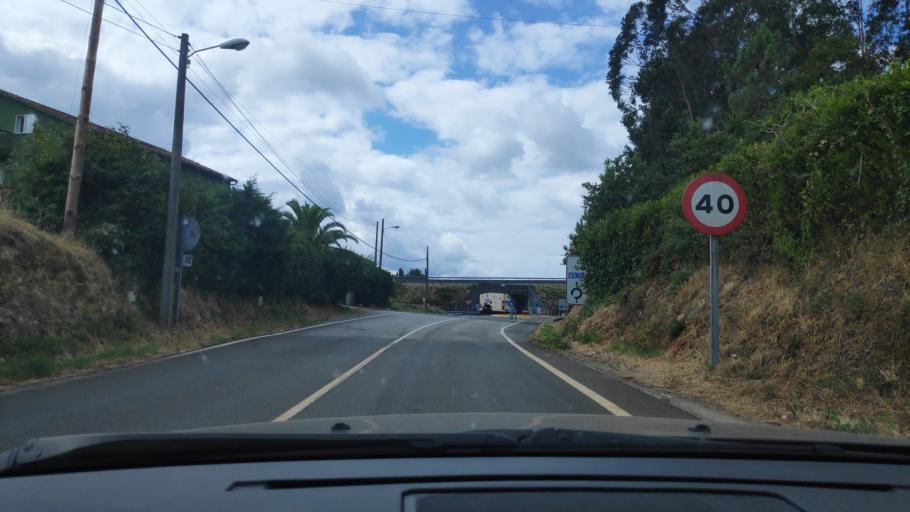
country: ES
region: Galicia
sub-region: Provincia da Coruna
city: Padron
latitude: 42.7274
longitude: -8.6744
